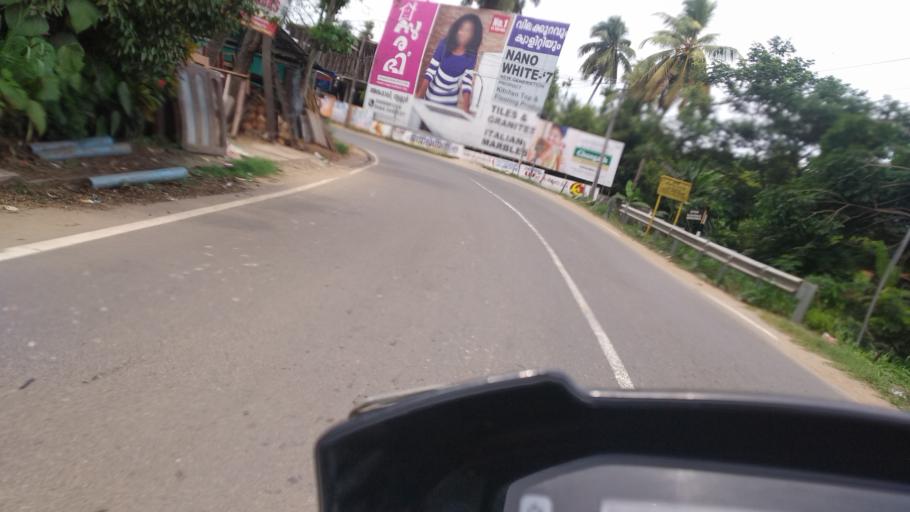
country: IN
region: Kerala
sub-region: Ernakulam
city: Aluva
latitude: 10.1565
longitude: 76.3269
